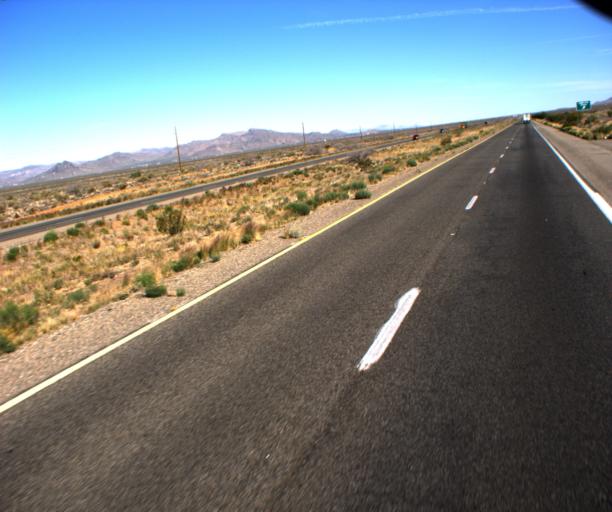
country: US
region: Arizona
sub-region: Mohave County
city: Golden Valley
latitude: 35.2919
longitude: -114.1831
